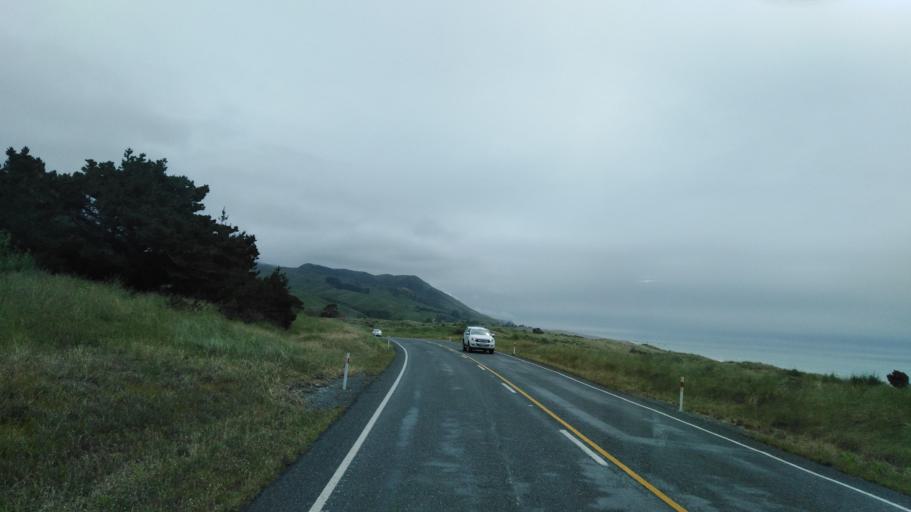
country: NZ
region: Marlborough
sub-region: Marlborough District
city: Blenheim
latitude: -41.9689
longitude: 174.0472
